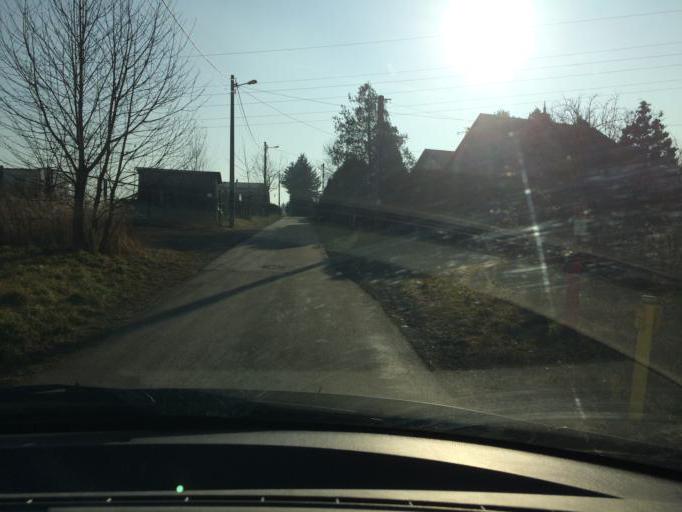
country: PL
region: Lesser Poland Voivodeship
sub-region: Powiat wielicki
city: Czarnochowice
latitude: 50.0057
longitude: 20.0417
